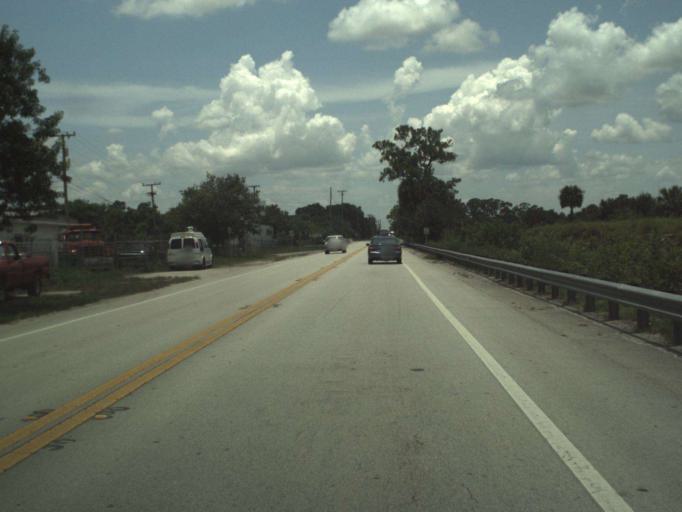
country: US
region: Florida
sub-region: Saint Lucie County
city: Lakewood Park
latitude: 27.4795
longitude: -80.3989
